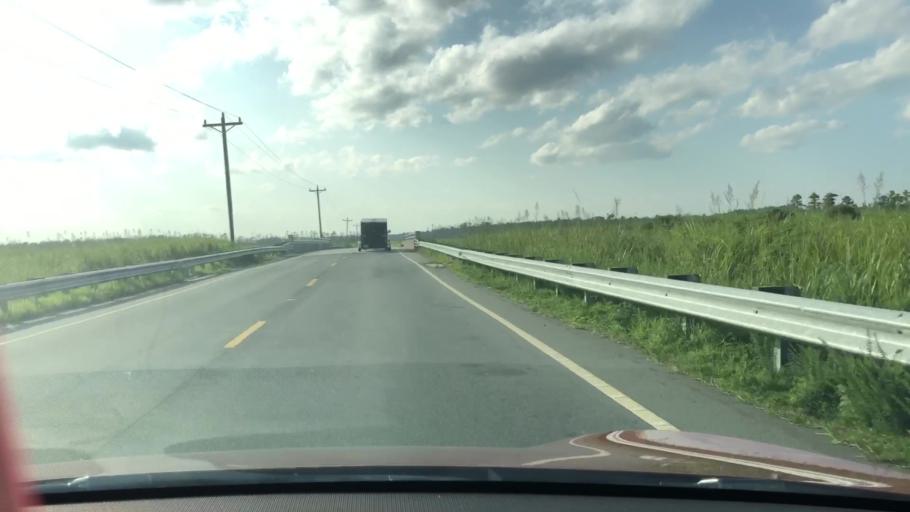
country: US
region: North Carolina
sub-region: Dare County
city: Wanchese
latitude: 35.6310
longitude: -75.8544
